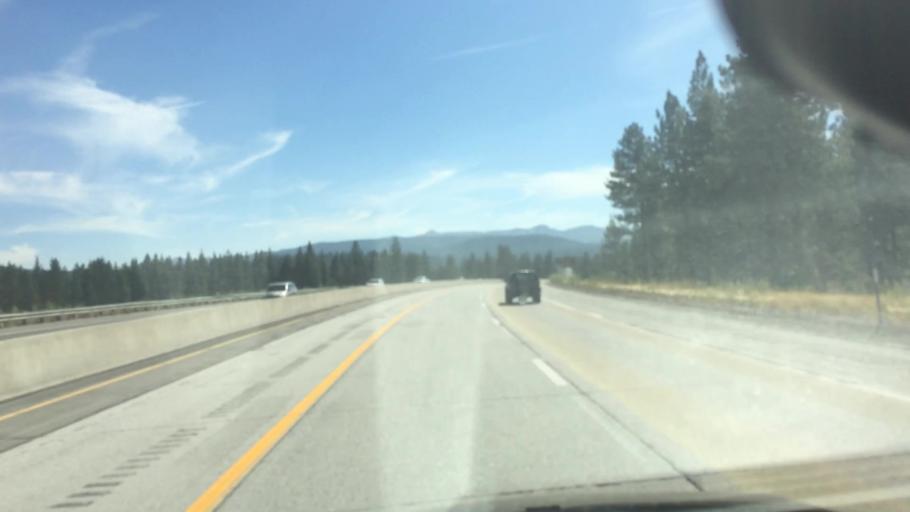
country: US
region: California
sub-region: Nevada County
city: Truckee
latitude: 39.3397
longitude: -120.1657
